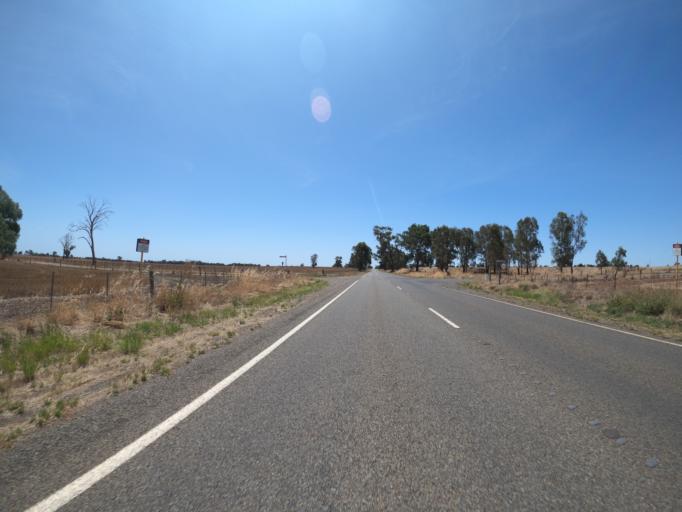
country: AU
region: Victoria
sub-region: Moira
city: Yarrawonga
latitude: -36.0555
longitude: 145.9954
